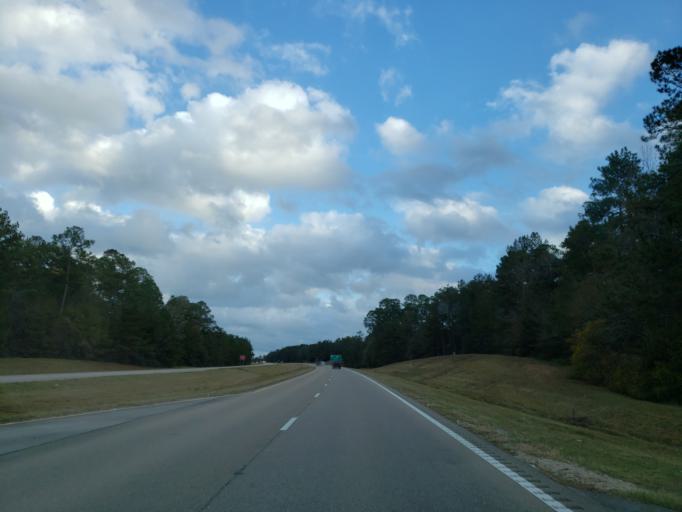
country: US
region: Mississippi
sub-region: Perry County
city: New Augusta
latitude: 31.1568
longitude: -88.9178
